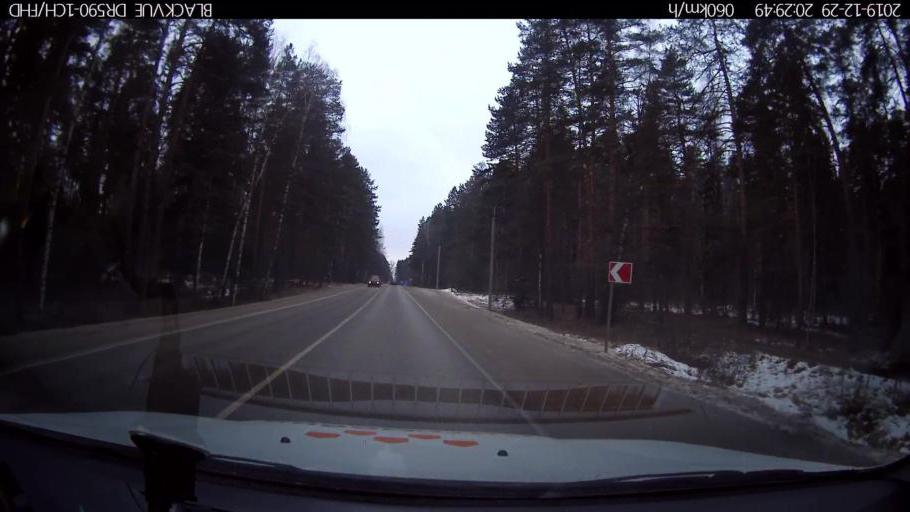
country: RU
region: Nizjnij Novgorod
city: Afonino
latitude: 56.1781
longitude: 44.0988
